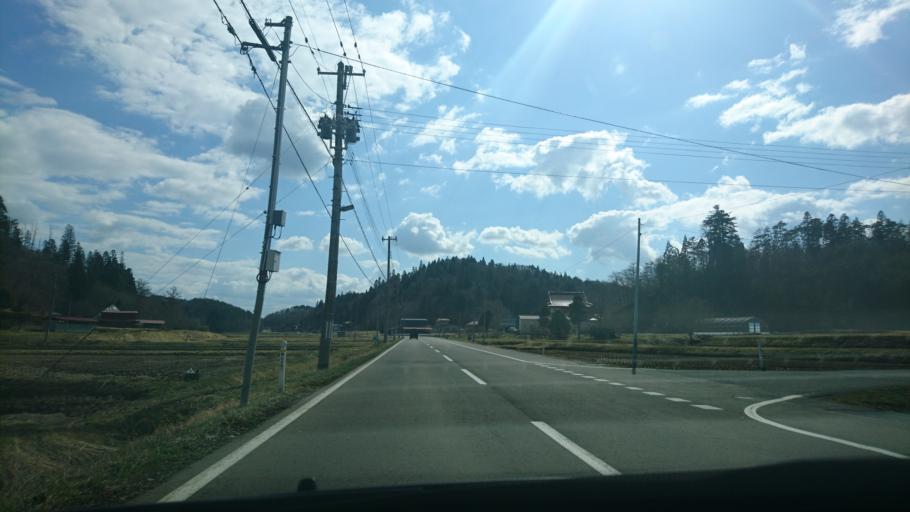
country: JP
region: Iwate
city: Kitakami
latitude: 39.3189
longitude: 141.2171
